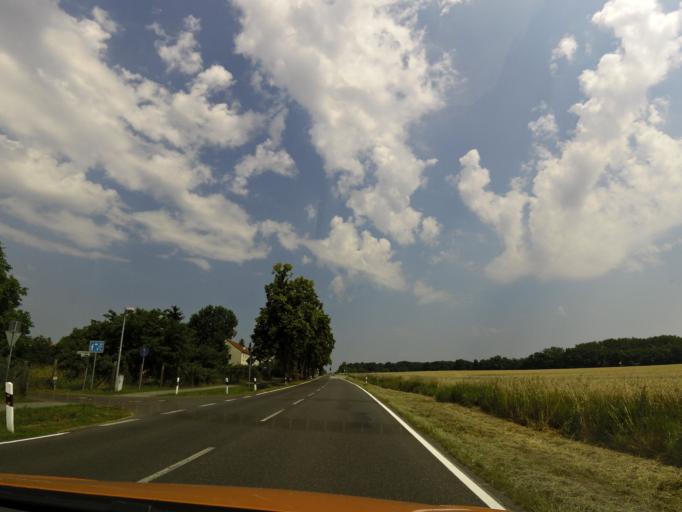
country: DE
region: Brandenburg
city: Wustermark
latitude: 52.5002
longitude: 12.9242
